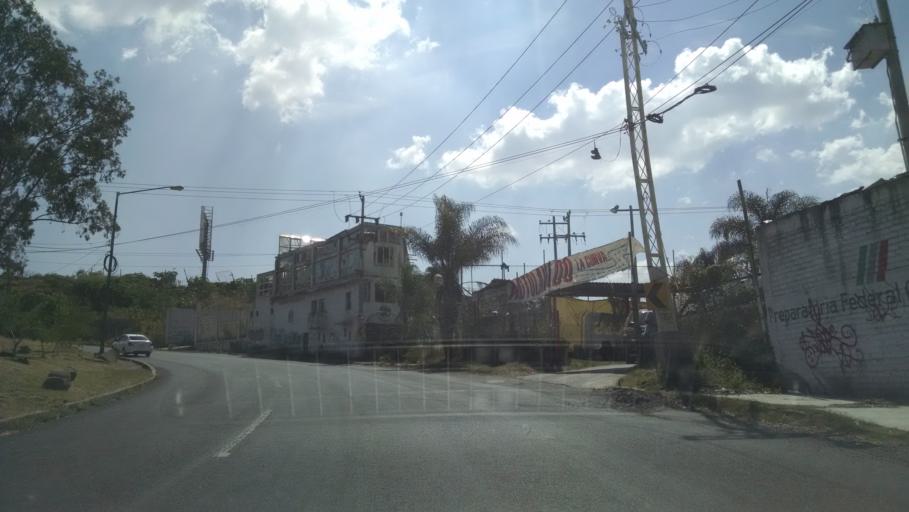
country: MX
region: Guanajuato
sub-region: Leon
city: La Ermita
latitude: 21.1371
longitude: -101.7210
